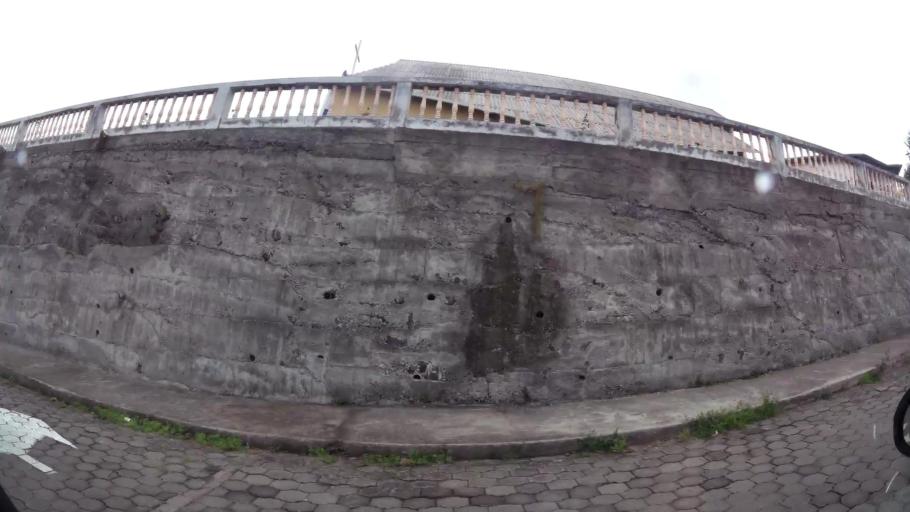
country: EC
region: Pichincha
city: Sangolqui
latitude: -0.2757
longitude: -78.4709
